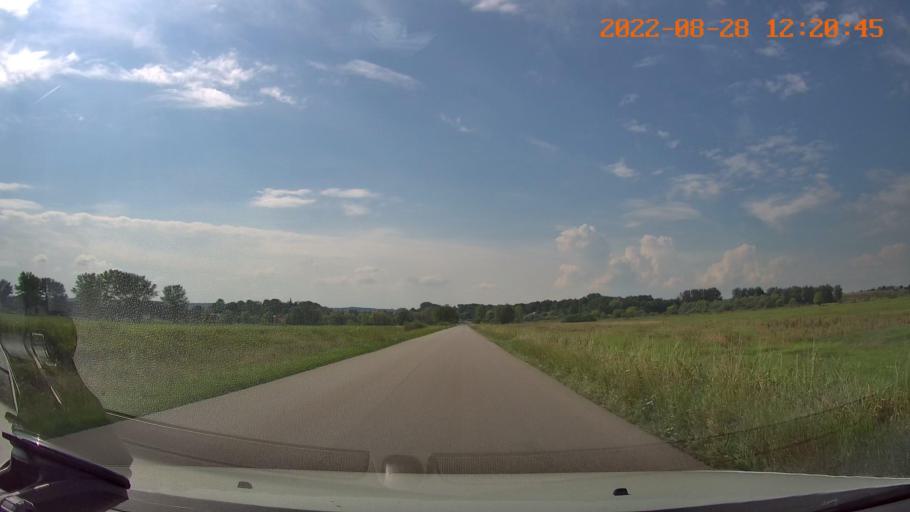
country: PL
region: Swietokrzyskie
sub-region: Powiat pinczowski
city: Zlota
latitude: 50.4283
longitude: 20.5655
